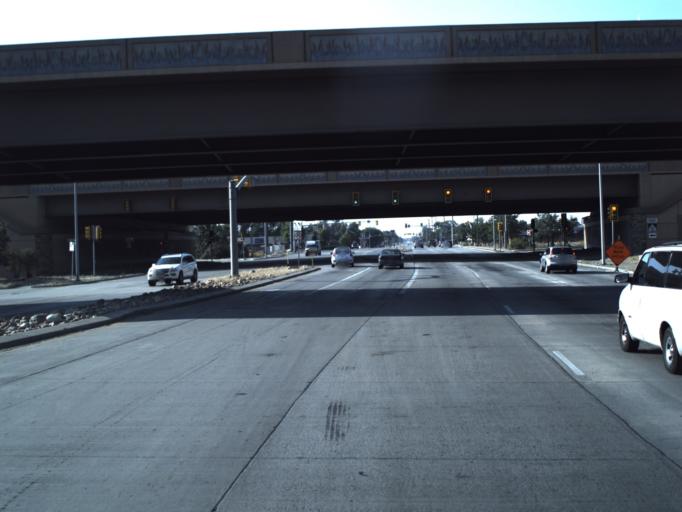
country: US
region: Utah
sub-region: Salt Lake County
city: South Salt Lake
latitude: 40.7250
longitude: -111.9391
